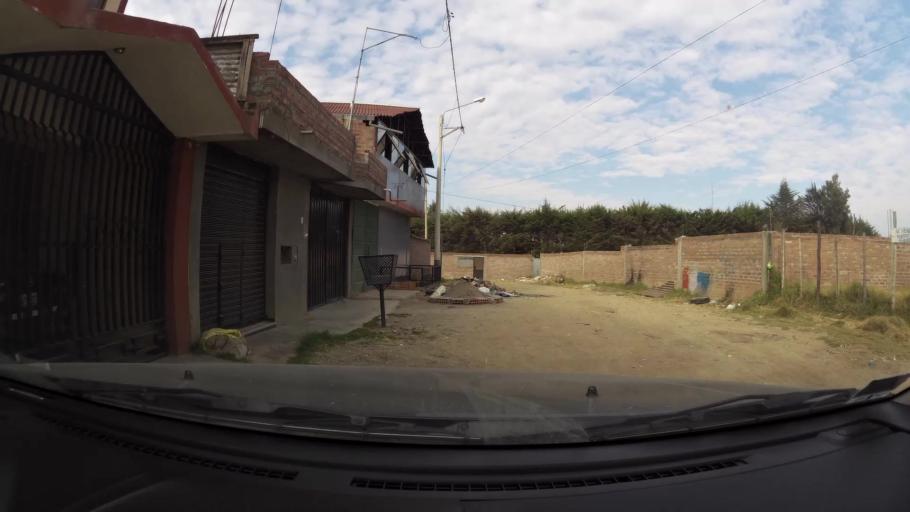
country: PE
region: Junin
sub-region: Provincia de Huancayo
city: Huancayo
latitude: -12.0453
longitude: -75.1959
